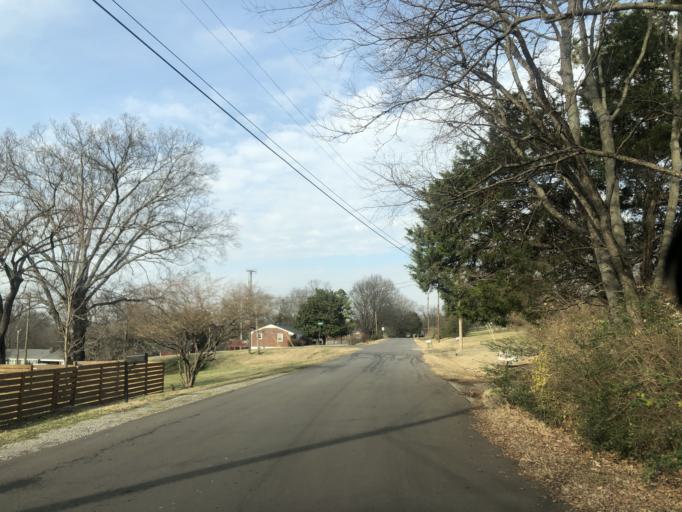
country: US
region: Tennessee
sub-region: Davidson County
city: Oak Hill
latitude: 36.1033
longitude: -86.7060
